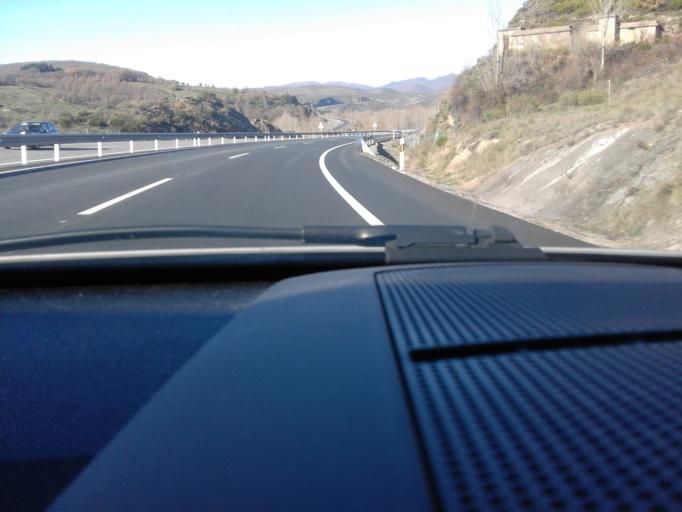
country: ES
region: Castille and Leon
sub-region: Provincia de Leon
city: Carrocera
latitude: 42.7855
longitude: -5.8021
